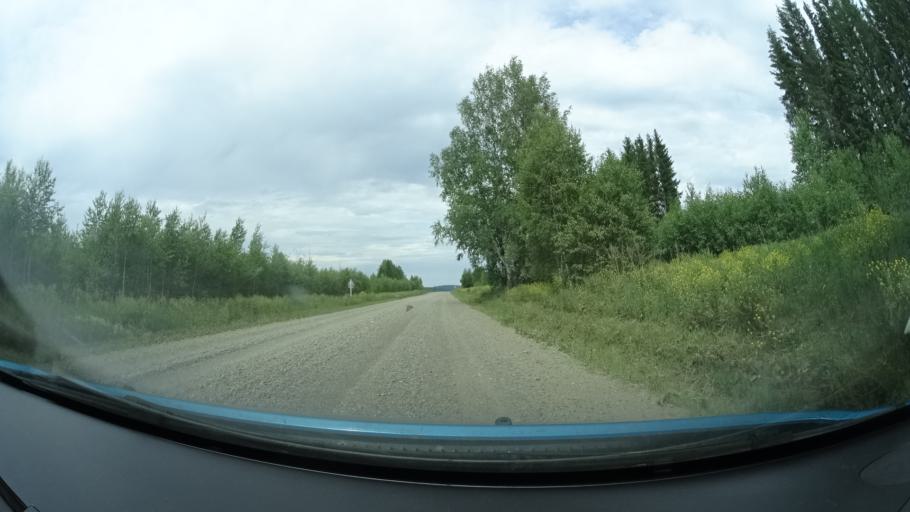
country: RU
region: Perm
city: Barda
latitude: 56.7865
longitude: 55.6733
